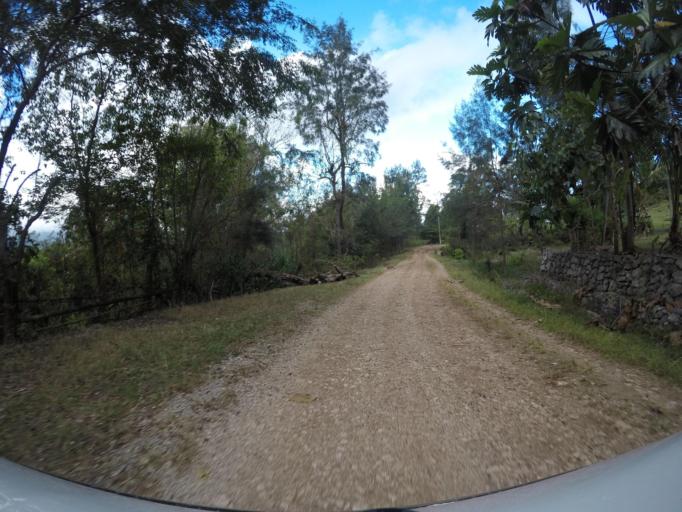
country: TL
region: Baucau
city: Venilale
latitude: -8.6849
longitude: 126.6543
